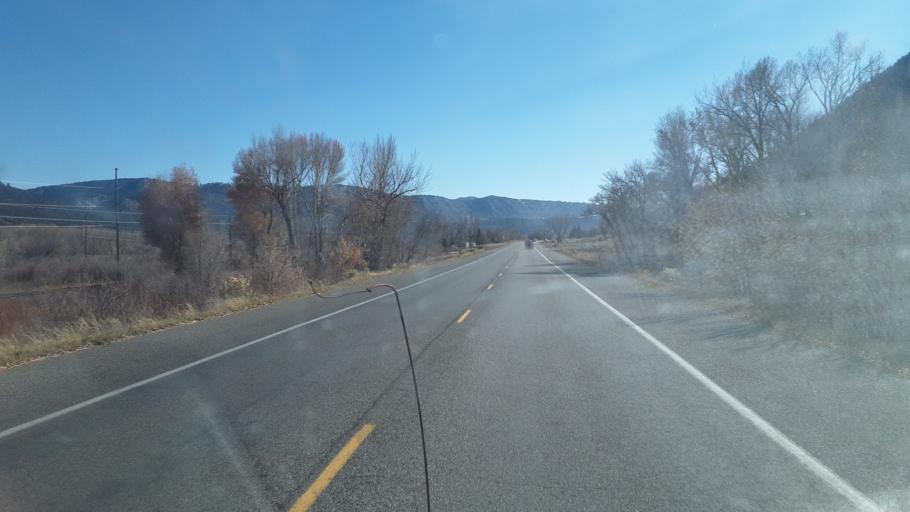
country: US
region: Colorado
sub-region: La Plata County
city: Durango
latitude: 37.3311
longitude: -107.8522
